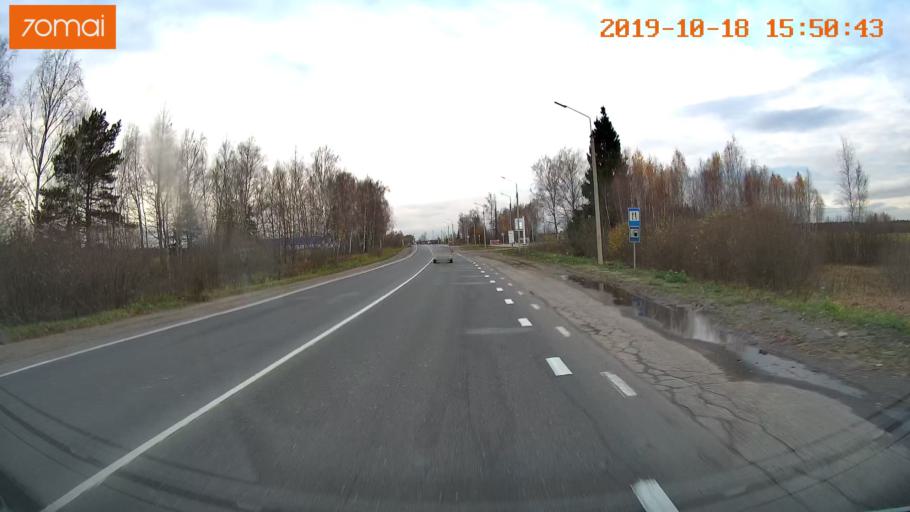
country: RU
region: Vladimir
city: Kommunar
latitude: 56.0353
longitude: 40.5565
